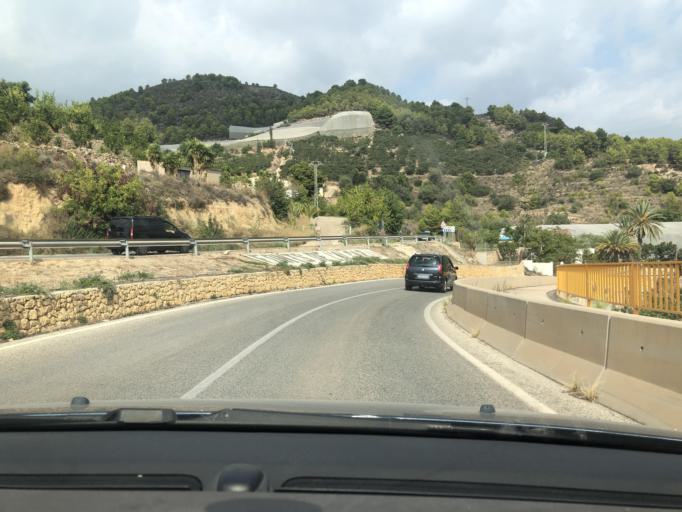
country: ES
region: Valencia
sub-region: Provincia de Alicante
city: Callosa d'En Sarria
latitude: 38.6547
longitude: -0.1067
